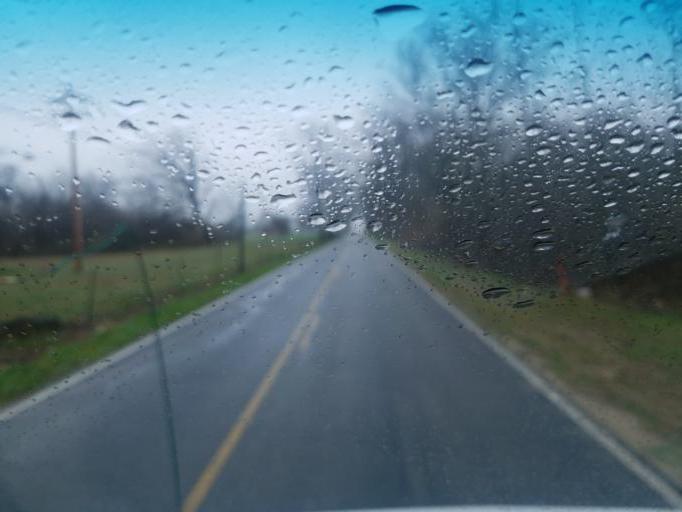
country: US
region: Ohio
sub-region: Wood County
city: North Baltimore
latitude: 41.1891
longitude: -83.6310
